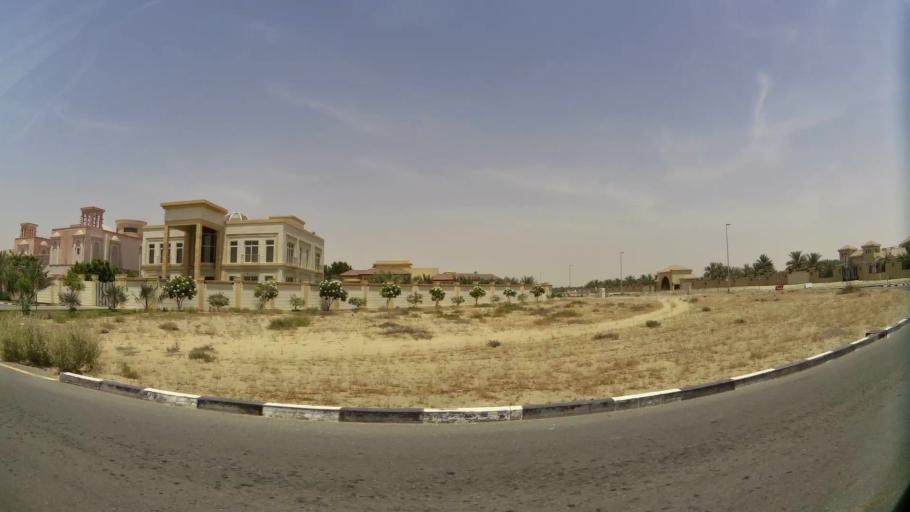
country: AE
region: Ash Shariqah
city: Sharjah
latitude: 25.2357
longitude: 55.4766
